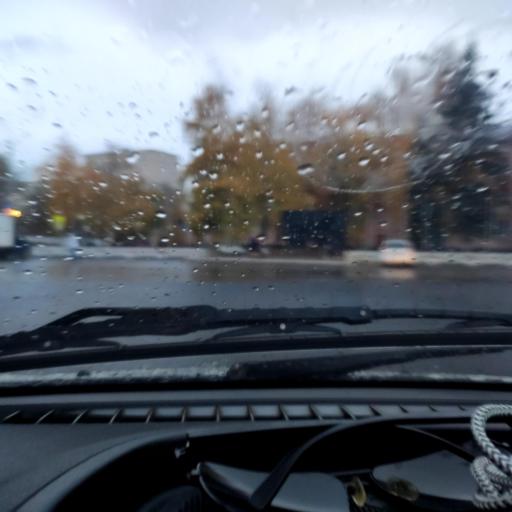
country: RU
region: Samara
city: Zhigulevsk
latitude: 53.4649
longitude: 49.5350
